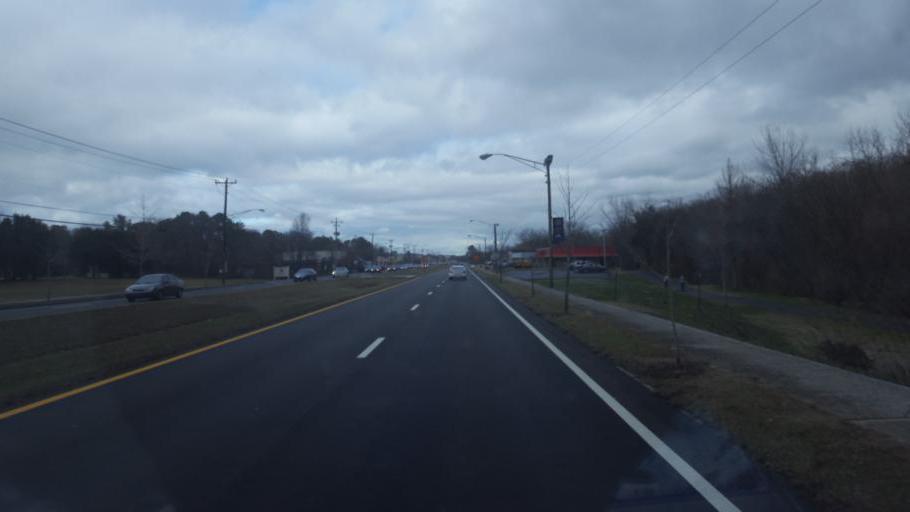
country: US
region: Tennessee
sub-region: Bradley County
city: Cleveland
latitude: 35.1763
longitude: -84.8766
